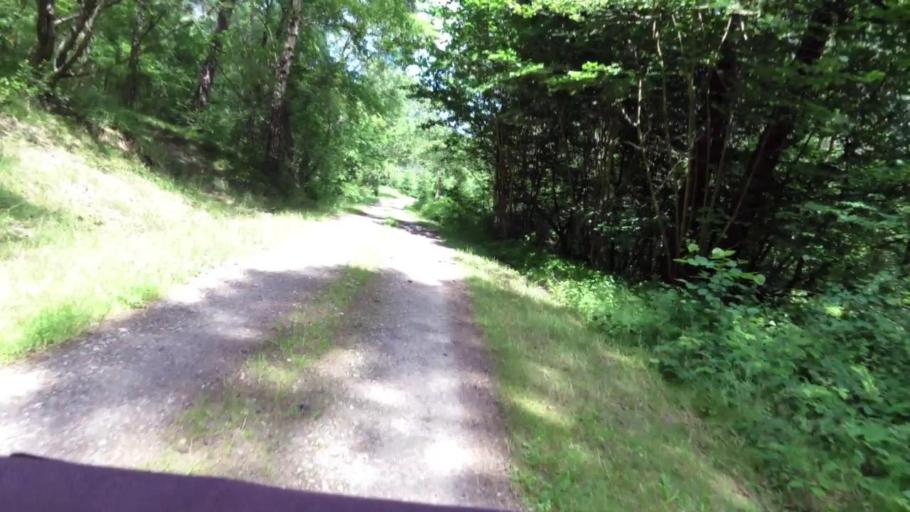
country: PL
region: West Pomeranian Voivodeship
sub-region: Powiat gryficki
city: Mrzezyno
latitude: 54.1261
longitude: 15.2467
